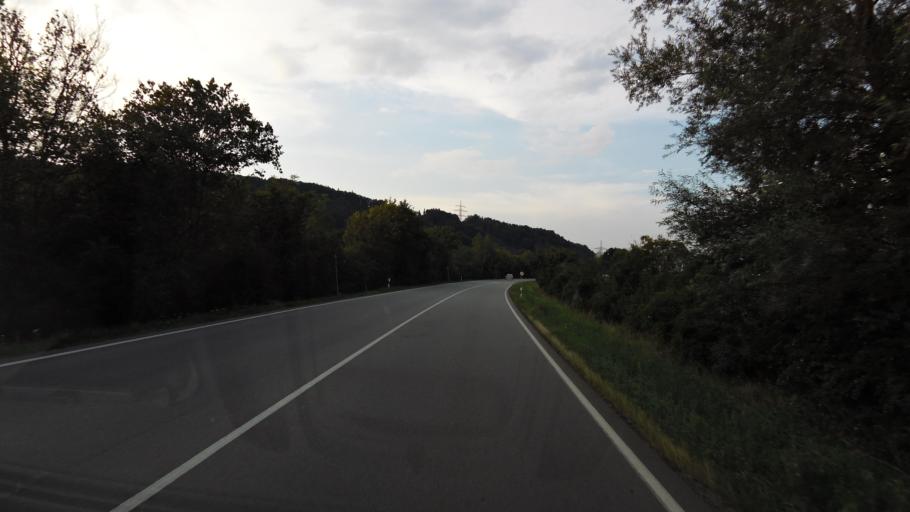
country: DE
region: Bavaria
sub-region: Lower Bavaria
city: Kirchdorf am Inn
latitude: 48.2603
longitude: 12.9985
